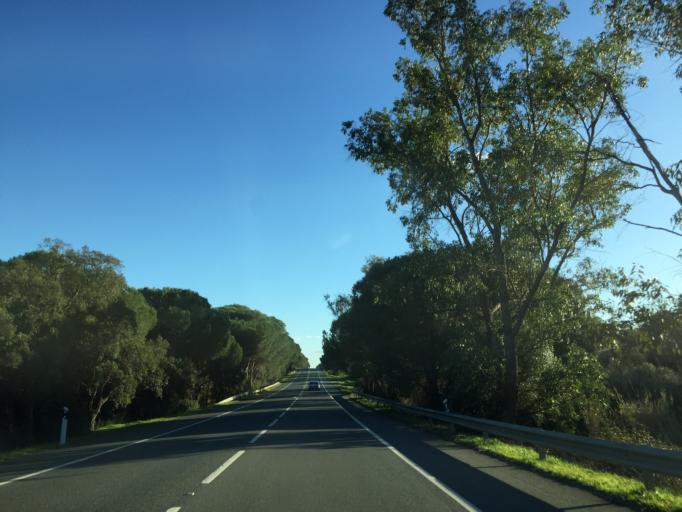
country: PT
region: Setubal
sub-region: Grandola
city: Grandola
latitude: 38.0890
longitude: -8.4180
